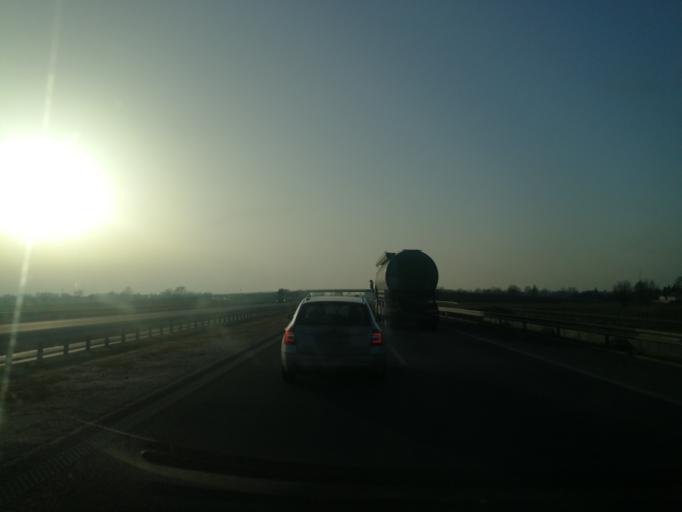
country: PL
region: Warmian-Masurian Voivodeship
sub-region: Powiat elblaski
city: Gronowo Elblaskie
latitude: 54.1646
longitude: 19.2755
